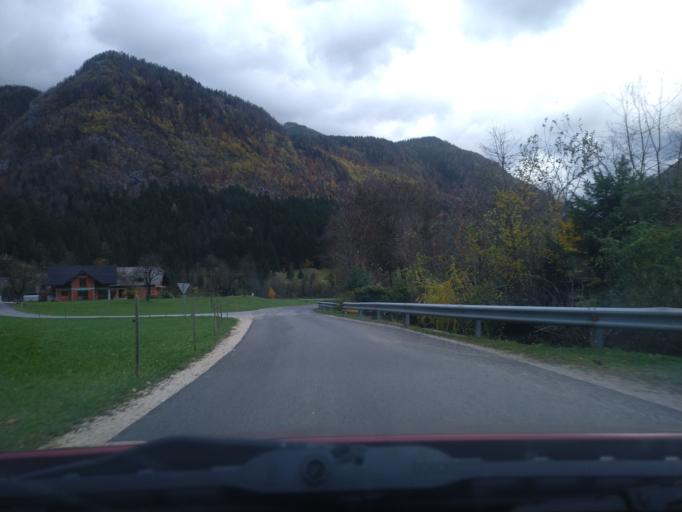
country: SI
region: Luce
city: Luce
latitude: 46.3138
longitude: 14.7017
